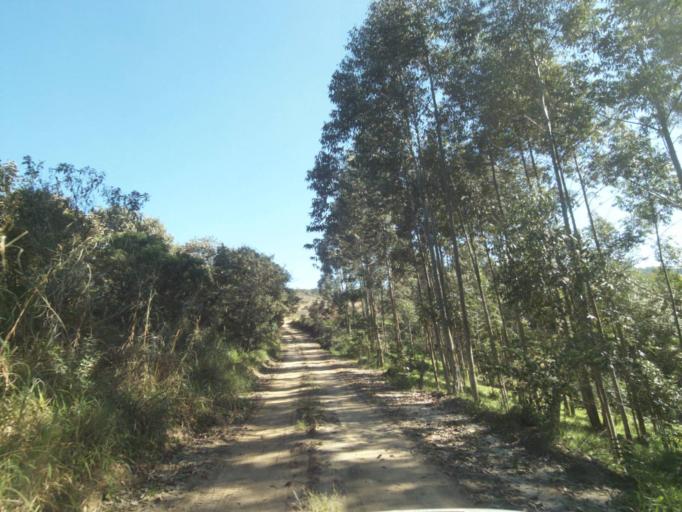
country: BR
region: Parana
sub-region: Tibagi
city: Tibagi
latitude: -24.5754
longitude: -50.4770
